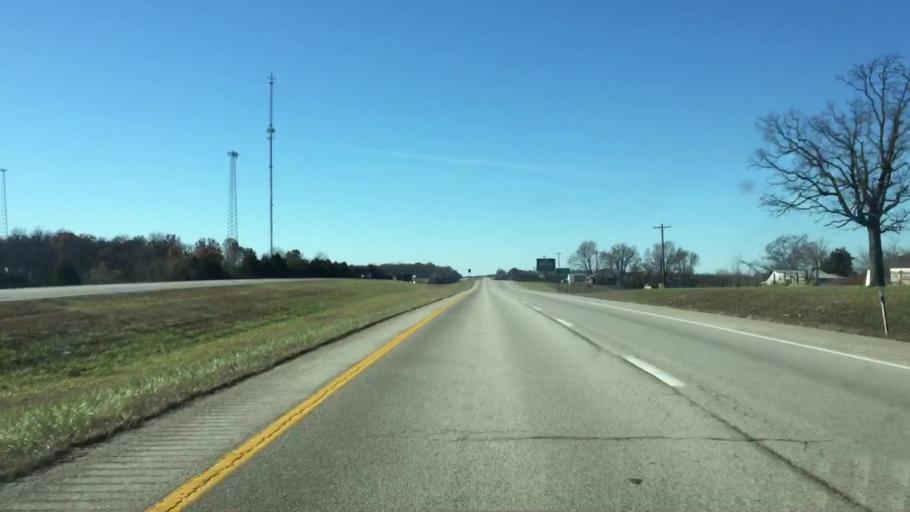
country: US
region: Missouri
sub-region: Cole County
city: Saint Martins
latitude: 38.4162
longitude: -92.3448
